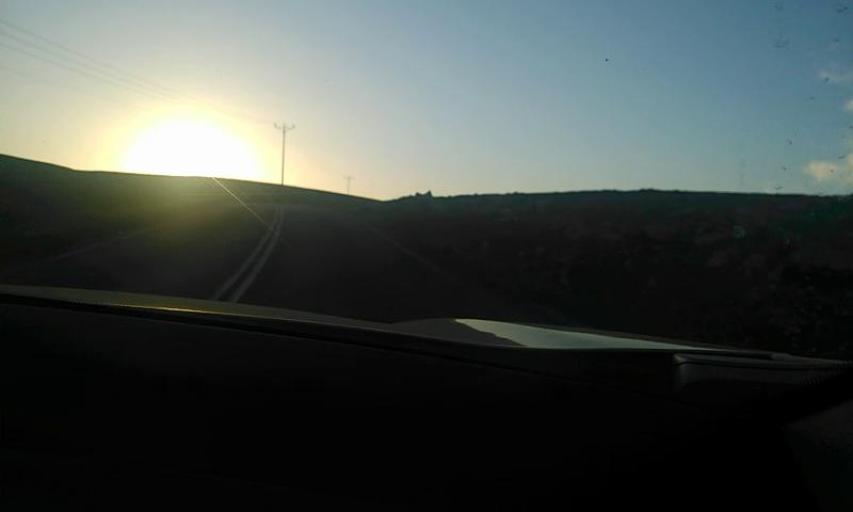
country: PS
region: West Bank
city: Rammun
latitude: 31.9178
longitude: 35.3418
